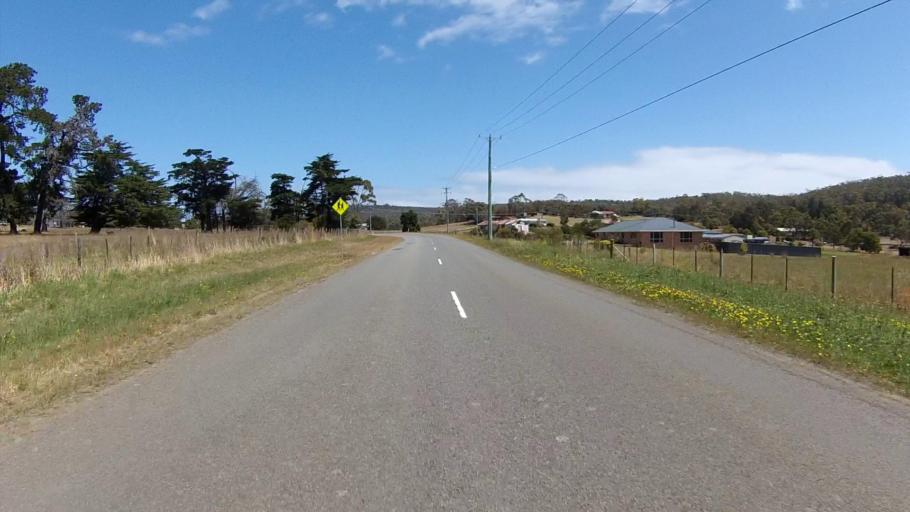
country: AU
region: Tasmania
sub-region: Clarence
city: Sandford
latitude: -42.9529
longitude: 147.4806
